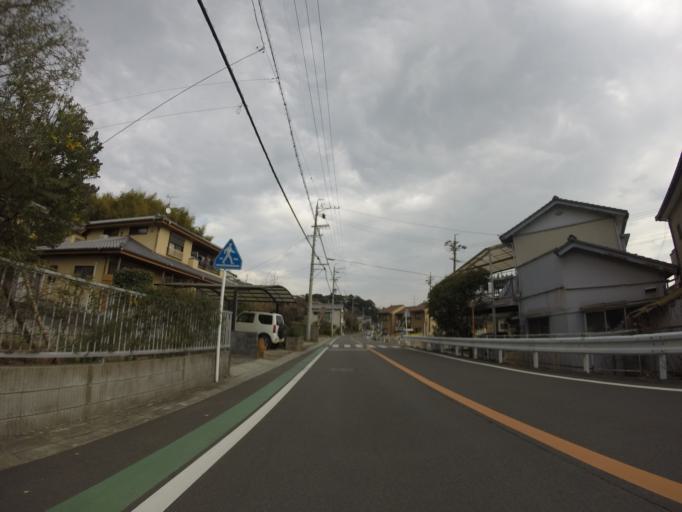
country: JP
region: Shizuoka
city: Shizuoka-shi
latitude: 35.0415
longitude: 138.4588
